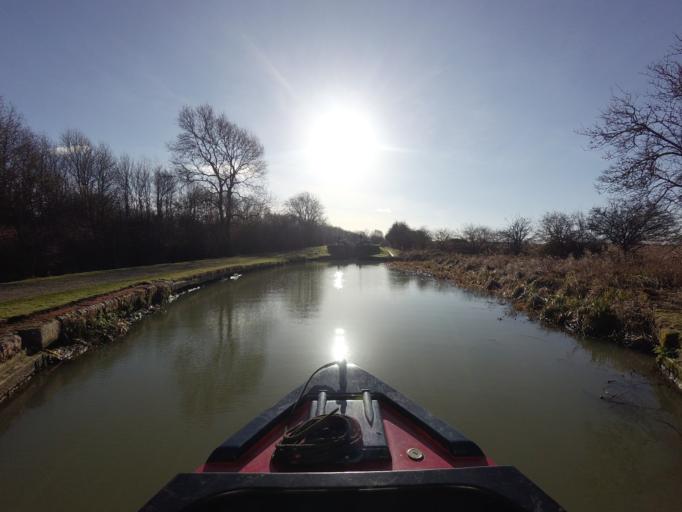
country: GB
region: England
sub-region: Northamptonshire
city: Blisworth
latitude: 52.2036
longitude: -0.9393
